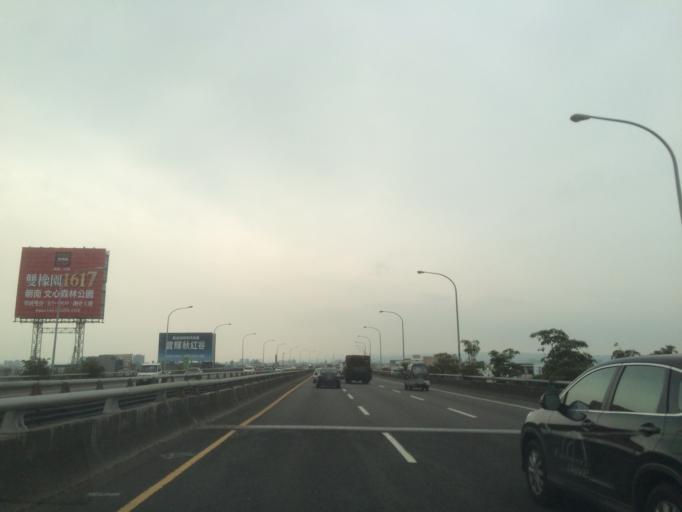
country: TW
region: Taiwan
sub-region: Taichung City
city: Taichung
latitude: 24.1415
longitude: 120.6228
